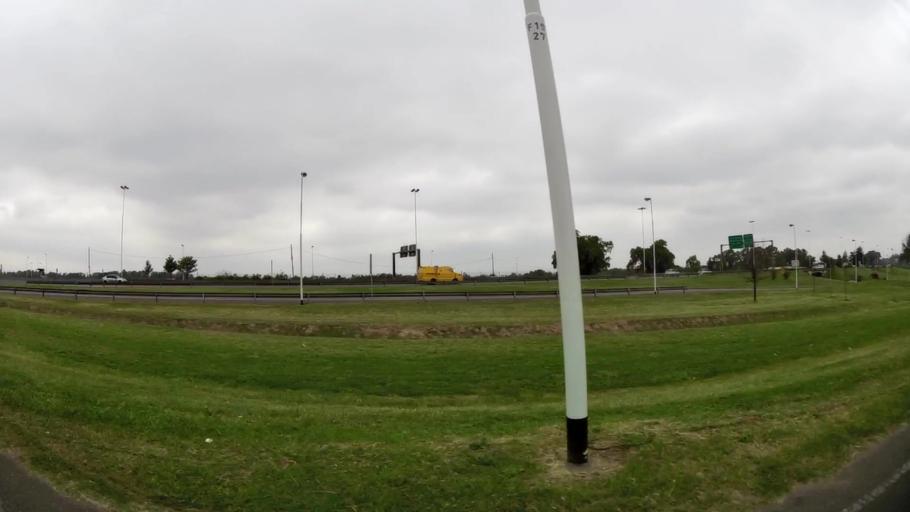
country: AR
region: Buenos Aires F.D.
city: Villa Lugano
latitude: -34.7256
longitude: -58.5159
